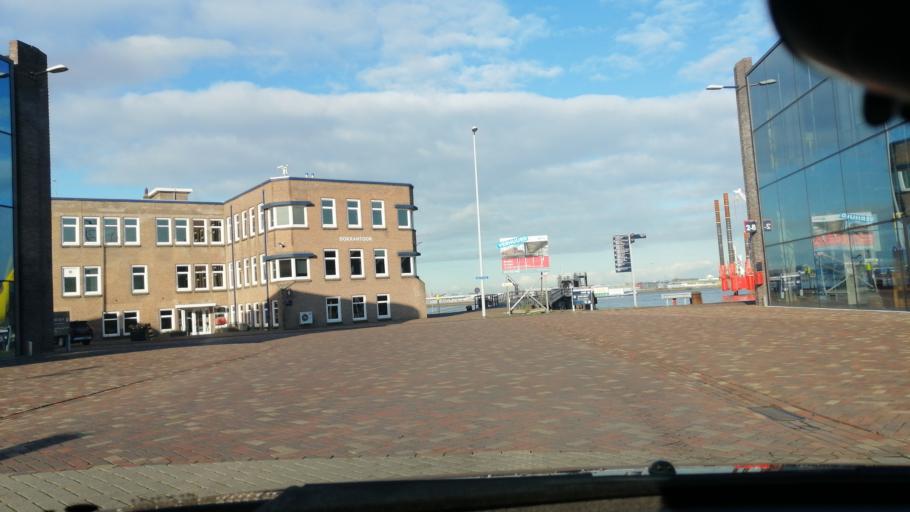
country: NL
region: South Holland
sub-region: Gemeente Rotterdam
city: Delfshaven
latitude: 51.8971
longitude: 4.4240
